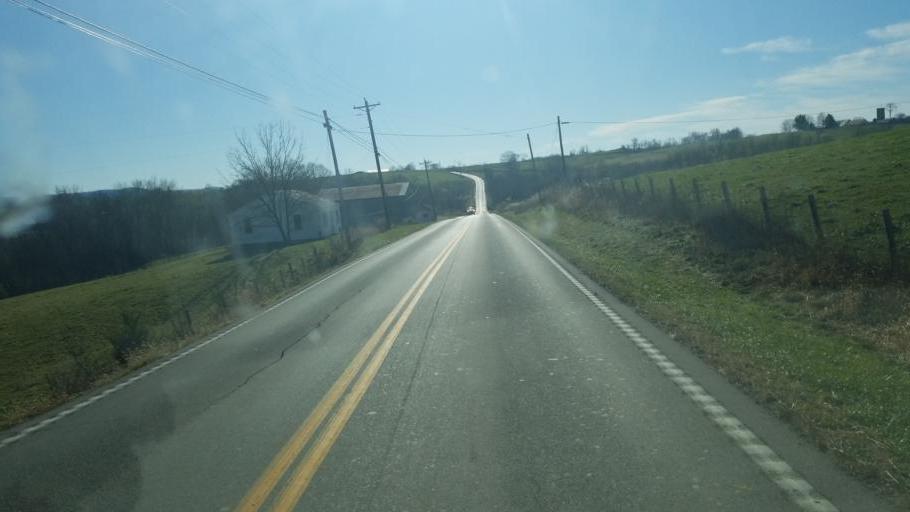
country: US
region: Kentucky
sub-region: Fleming County
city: Flemingsburg
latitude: 38.5071
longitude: -83.6220
